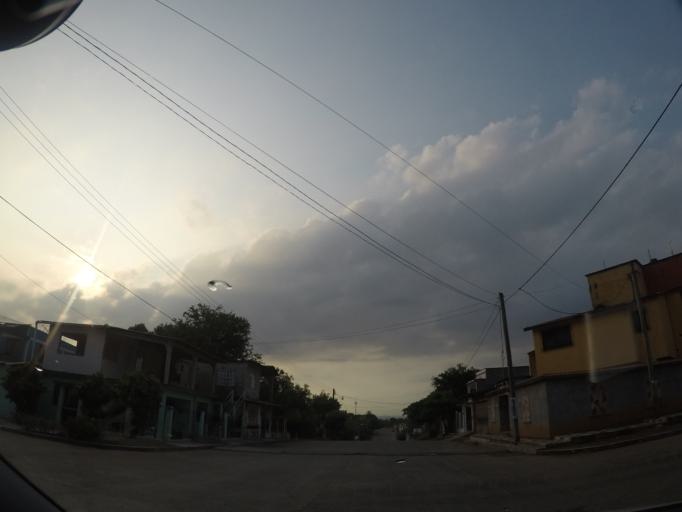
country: MX
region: Oaxaca
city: Matias Romero
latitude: 16.8719
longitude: -95.0408
